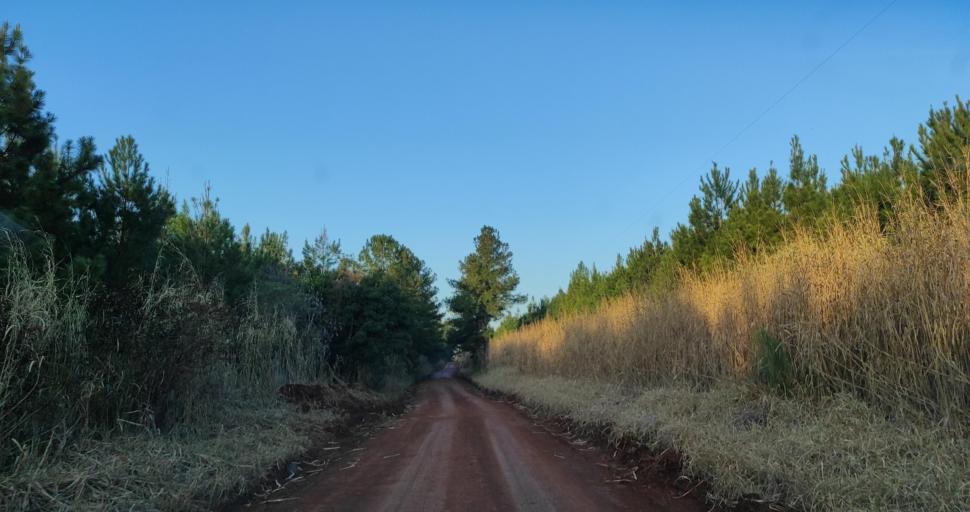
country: AR
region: Misiones
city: Capiovi
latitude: -26.8810
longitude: -55.1215
